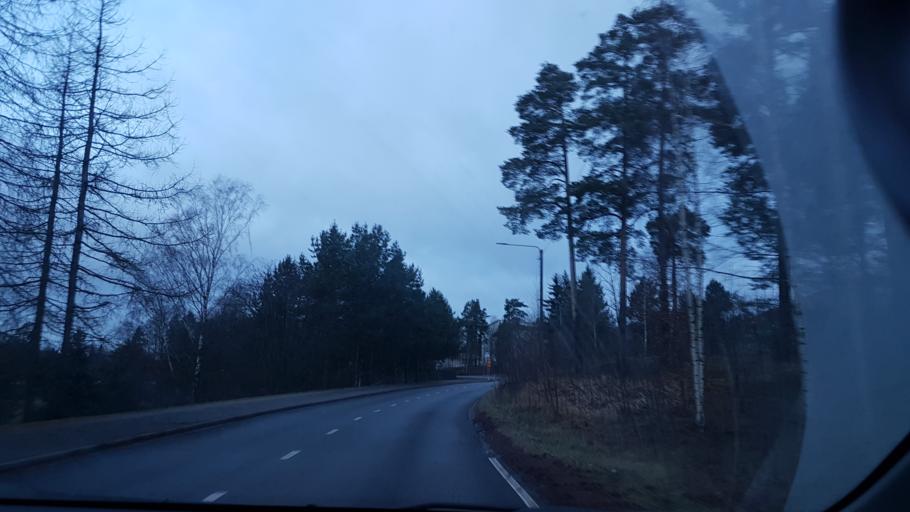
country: FI
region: Uusimaa
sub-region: Helsinki
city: Vantaa
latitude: 60.2810
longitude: 25.1227
